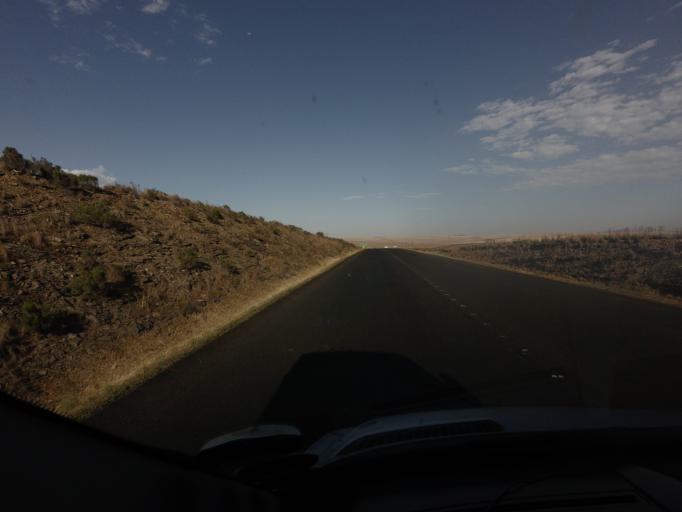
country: ZA
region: Western Cape
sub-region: Overberg District Municipality
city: Swellendam
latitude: -34.1069
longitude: 20.3452
